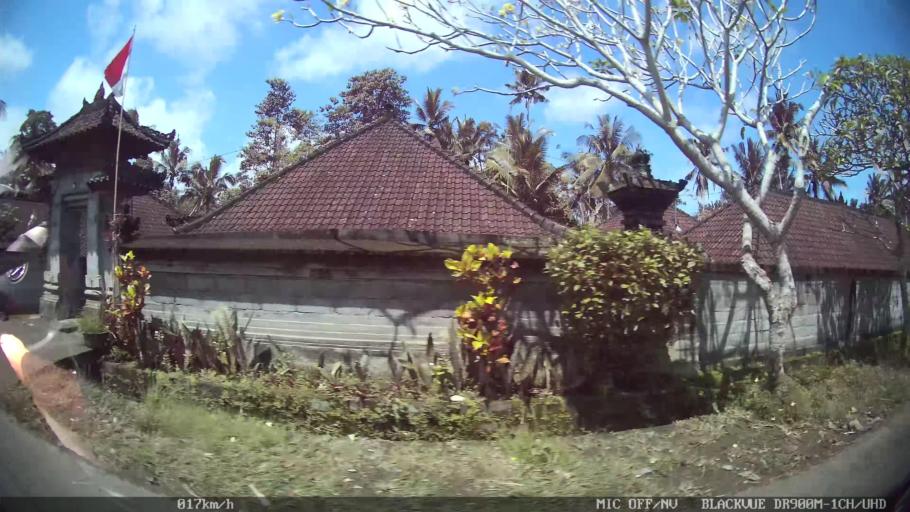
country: ID
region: Bali
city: Banjar Kelodan
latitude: -8.5142
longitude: 115.3344
